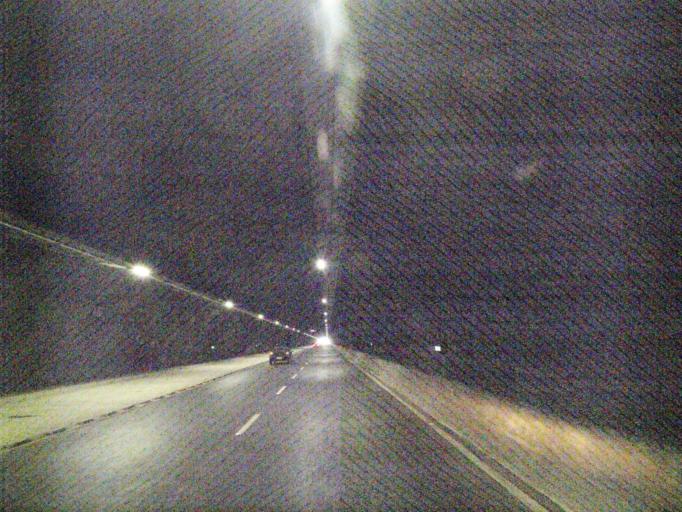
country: BR
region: Rio de Janeiro
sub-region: Niteroi
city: Niteroi
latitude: -22.9343
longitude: -43.0912
